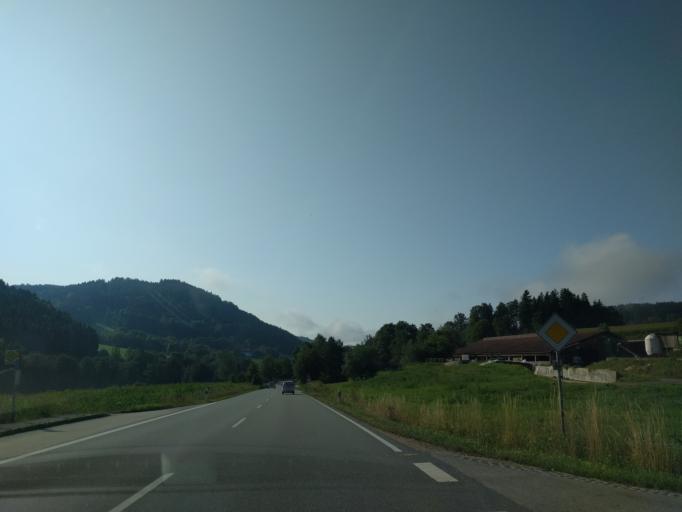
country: DE
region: Bavaria
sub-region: Lower Bavaria
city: Innernzell
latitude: 48.8536
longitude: 13.3044
